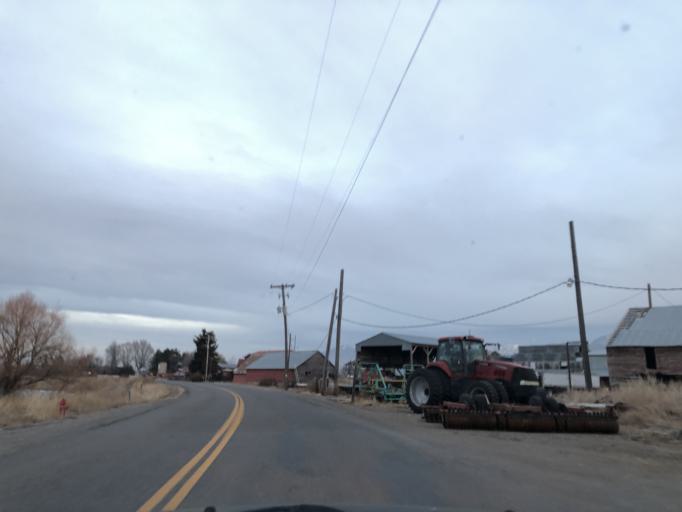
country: US
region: Utah
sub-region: Cache County
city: Benson
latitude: 41.7914
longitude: -111.9073
